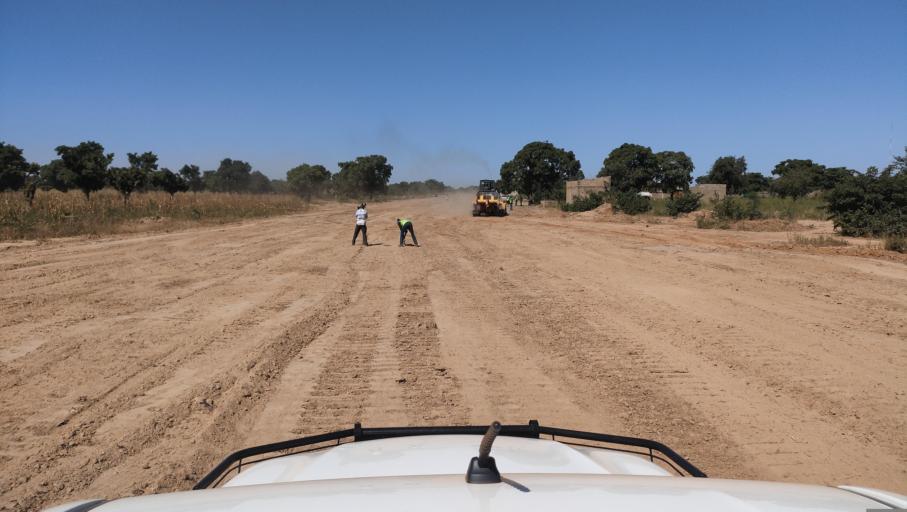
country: BF
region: Est
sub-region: Province du Gourma
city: Fada N'gourma
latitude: 12.0692
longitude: 0.3328
